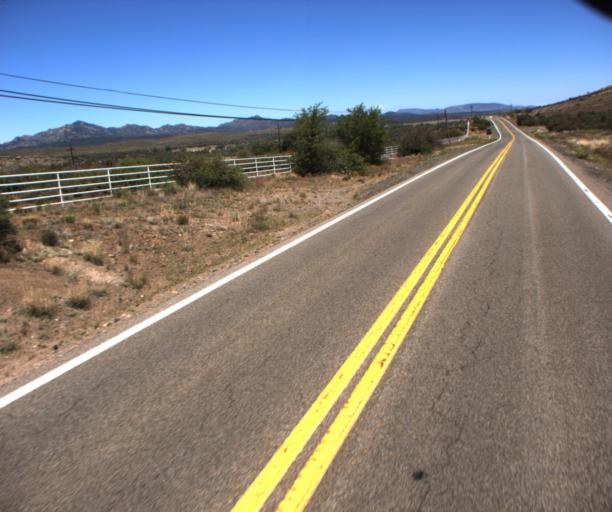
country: US
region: Arizona
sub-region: Yavapai County
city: Congress
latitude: 34.2406
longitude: -112.7367
